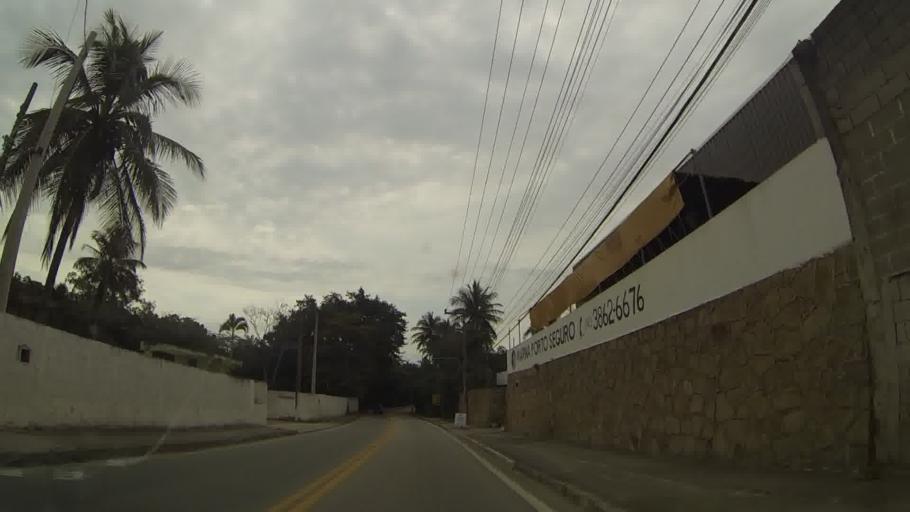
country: BR
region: Sao Paulo
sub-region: Sao Sebastiao
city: Sao Sebastiao
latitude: -23.8216
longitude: -45.4114
